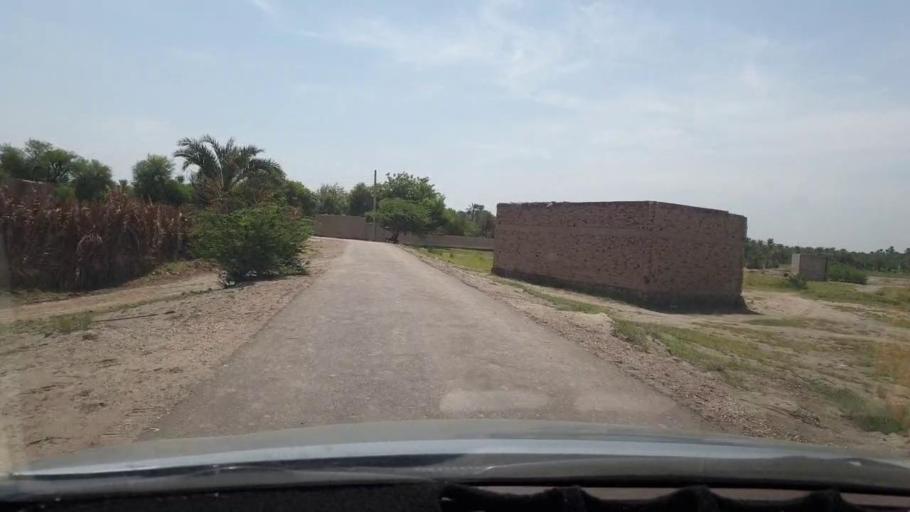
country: PK
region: Sindh
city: Khairpur
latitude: 27.4863
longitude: 68.7641
